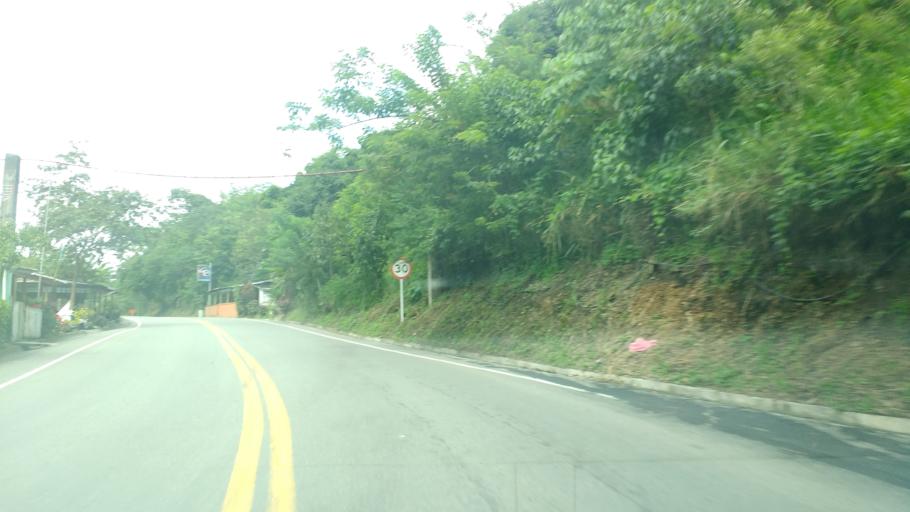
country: CO
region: Antioquia
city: Titiribi
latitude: 6.0614
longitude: -75.7505
